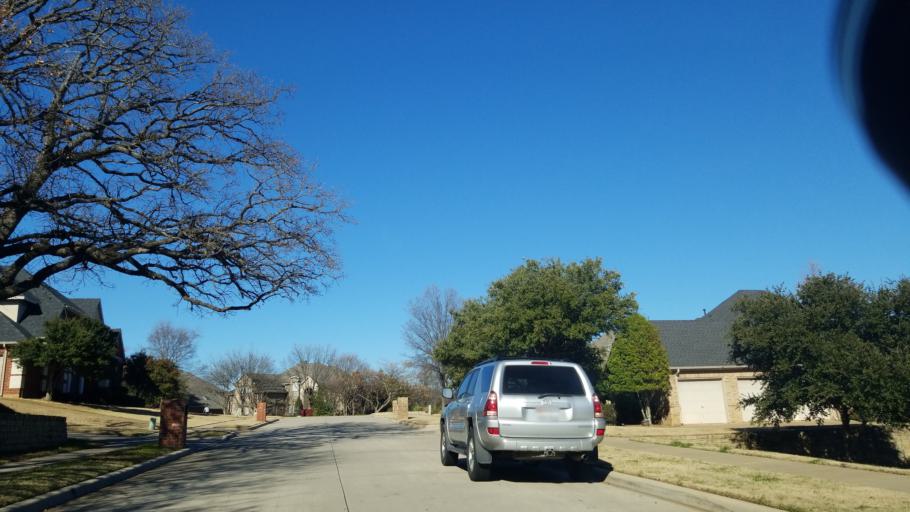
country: US
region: Texas
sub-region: Denton County
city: Corinth
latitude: 33.1526
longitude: -97.0870
